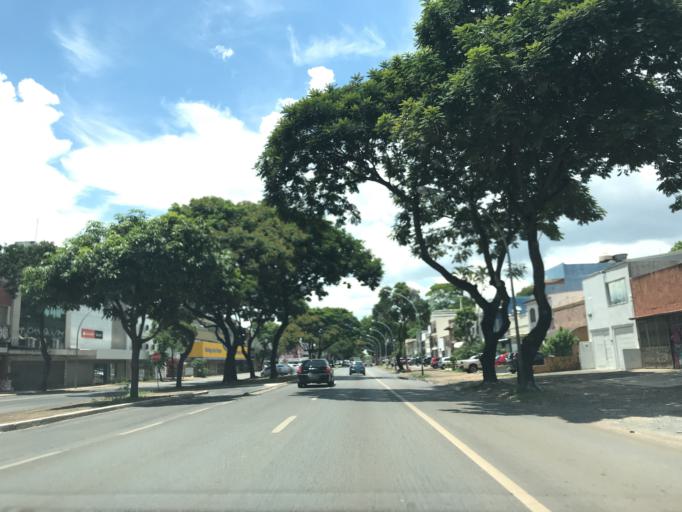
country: BR
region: Federal District
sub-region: Brasilia
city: Brasilia
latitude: -15.8022
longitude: -47.8953
